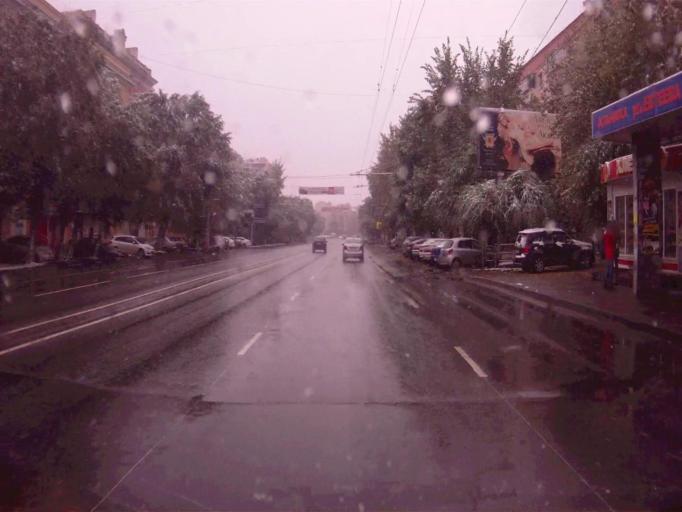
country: RU
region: Chelyabinsk
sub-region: Gorod Chelyabinsk
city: Chelyabinsk
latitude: 55.1500
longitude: 61.4156
